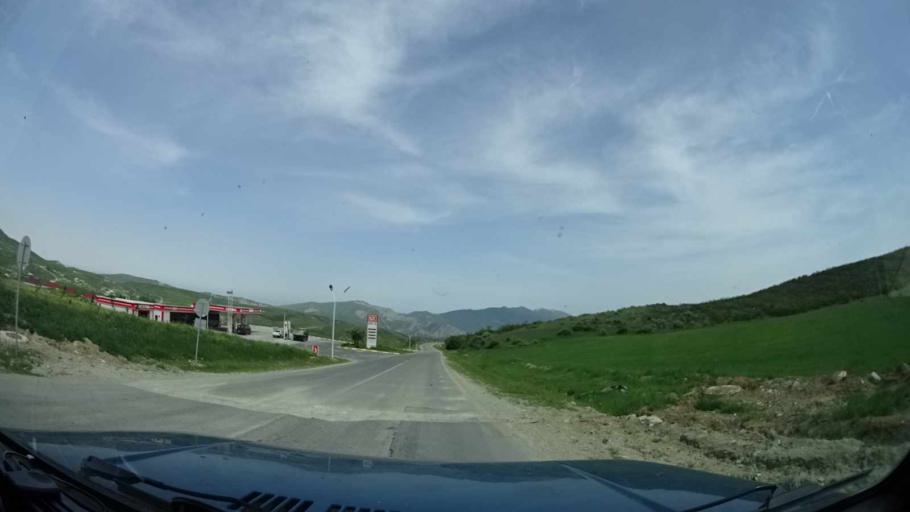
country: AZ
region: Xizi
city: Khyzy
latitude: 40.9071
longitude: 49.0933
